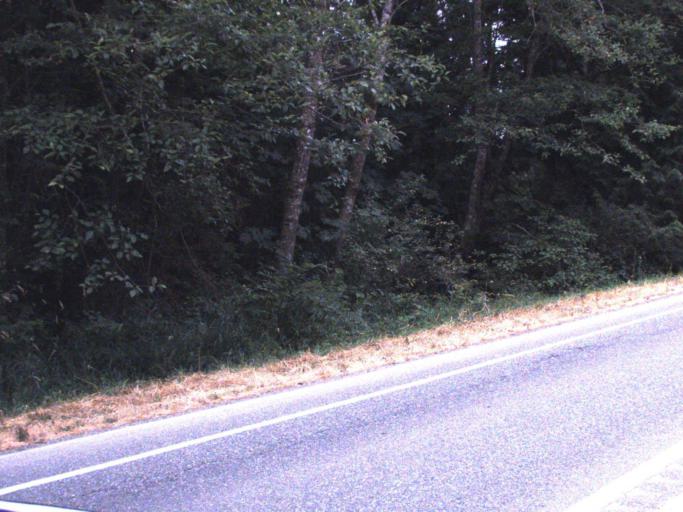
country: US
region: Washington
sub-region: King County
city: Ames Lake
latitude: 47.6220
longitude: -121.9634
